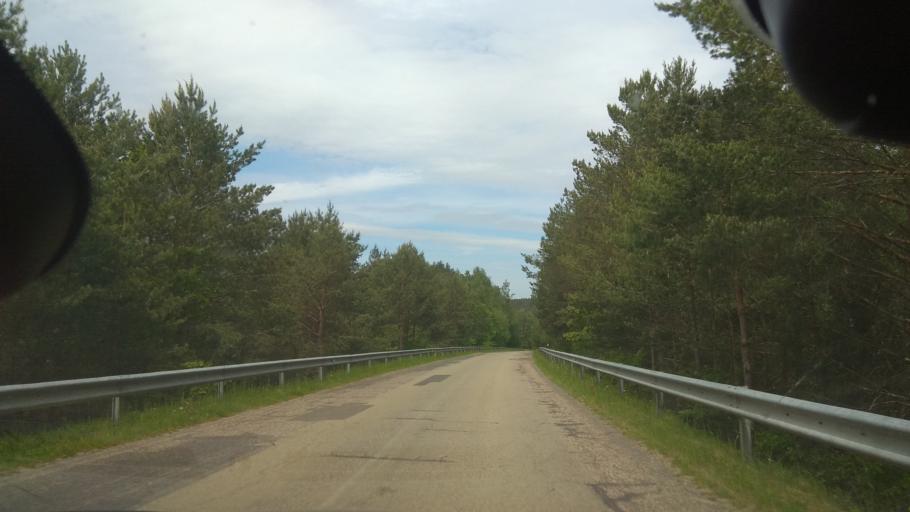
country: LT
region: Vilnius County
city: Ukmerge
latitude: 55.1327
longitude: 24.5965
